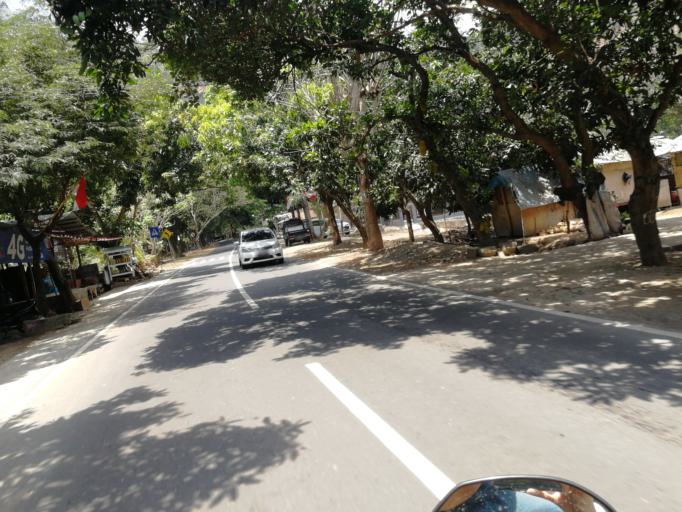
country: ID
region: West Nusa Tenggara
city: Karangsubagan
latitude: -8.4529
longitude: 116.0401
